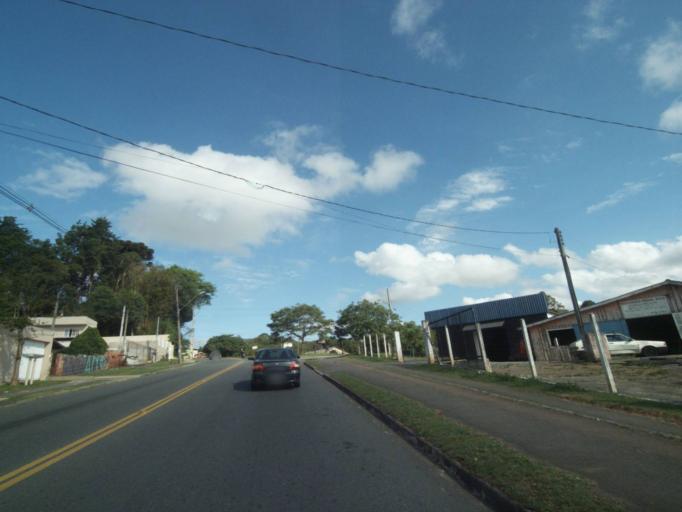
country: BR
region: Parana
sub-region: Curitiba
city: Curitiba
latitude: -25.3879
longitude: -49.3009
